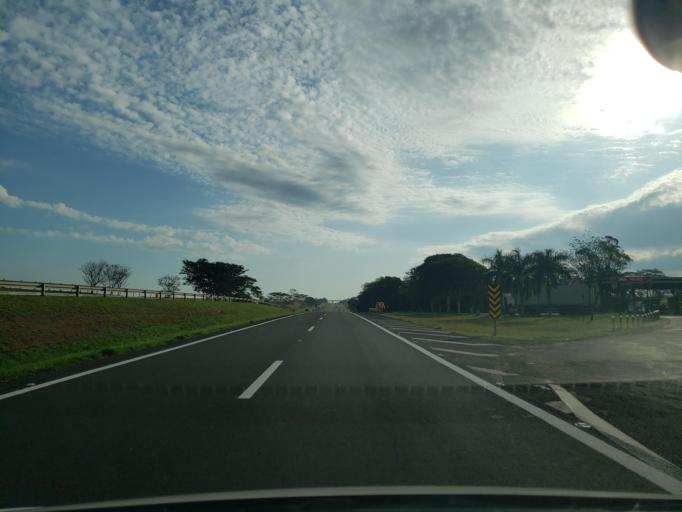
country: BR
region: Sao Paulo
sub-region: Valparaiso
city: Valparaiso
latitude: -21.2059
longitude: -50.7769
